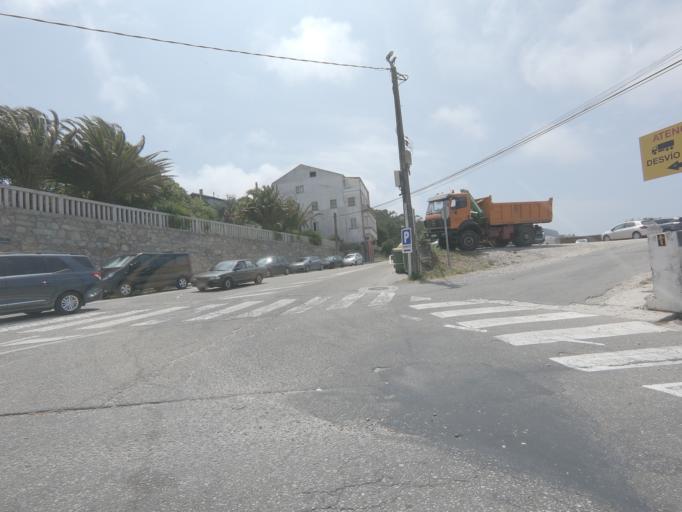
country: ES
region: Galicia
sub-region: Provincia de Pontevedra
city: A Guarda
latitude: 41.9030
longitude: -8.8664
